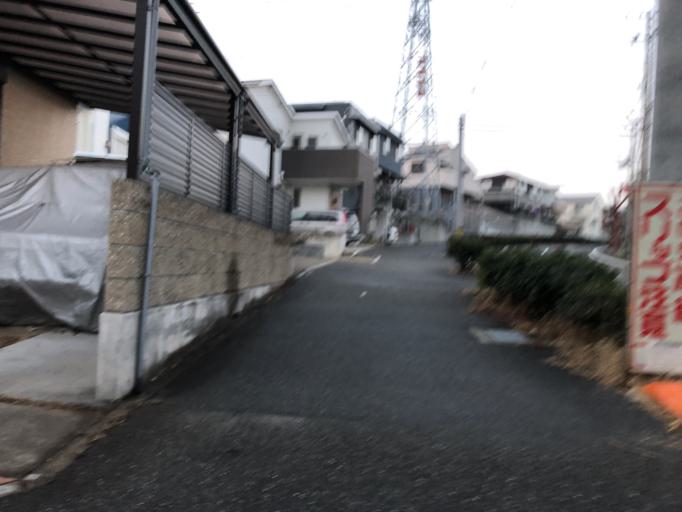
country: JP
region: Hyogo
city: Akashi
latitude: 34.6490
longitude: 135.0185
